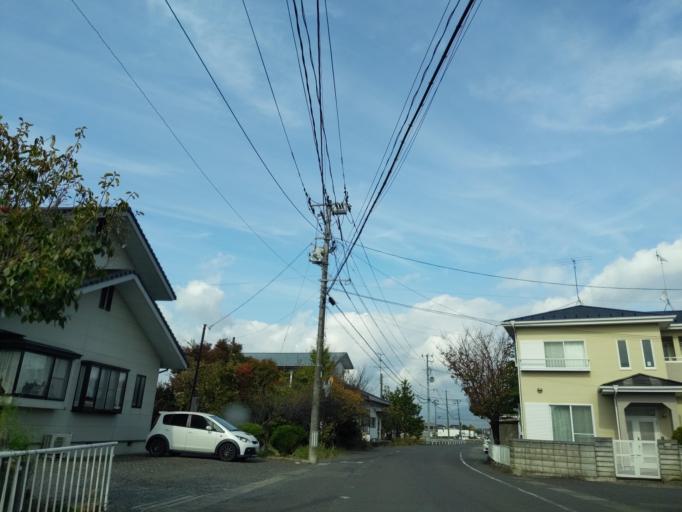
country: JP
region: Fukushima
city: Koriyama
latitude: 37.4309
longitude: 140.3344
